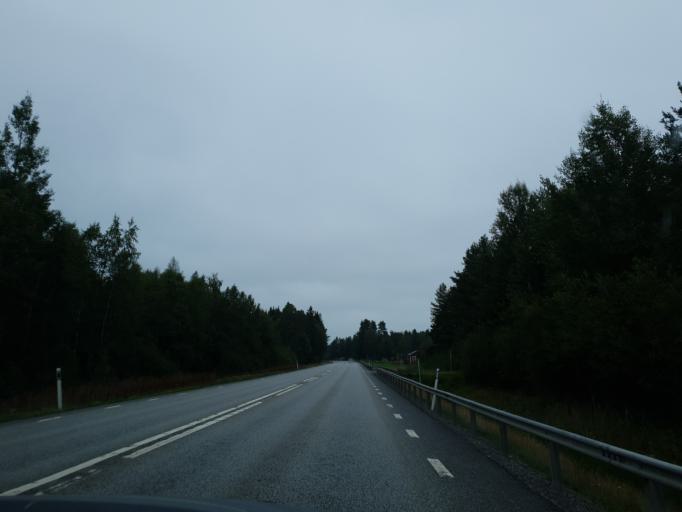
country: SE
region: Vaesterbotten
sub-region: Robertsfors Kommun
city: Robertsfors
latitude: 64.2518
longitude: 21.0413
